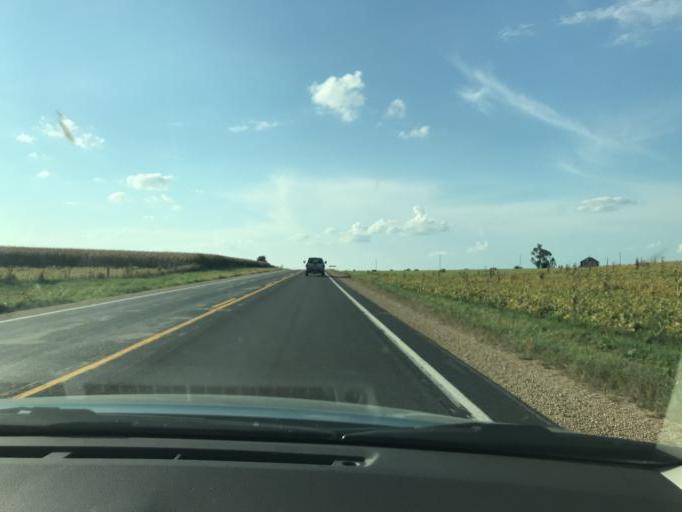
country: US
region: Wisconsin
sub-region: Grant County
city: Platteville
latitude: 42.7079
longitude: -90.4474
